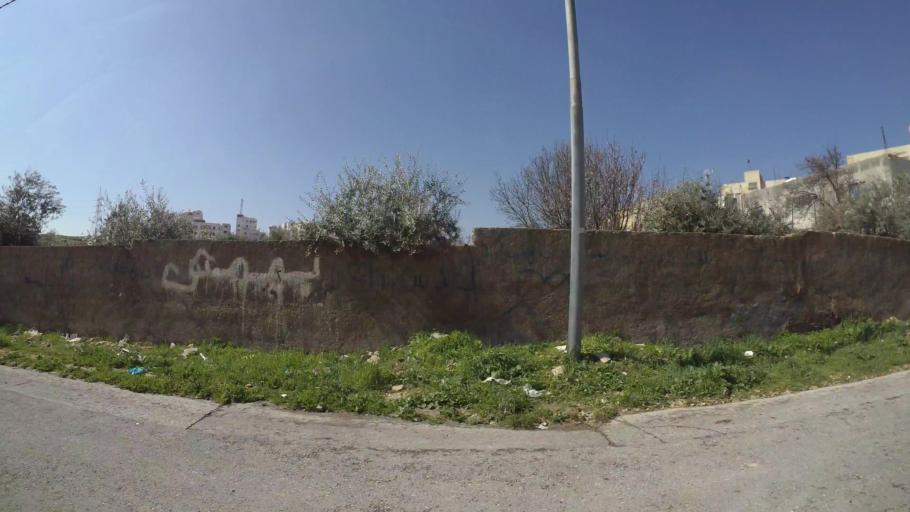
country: JO
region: Amman
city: Al Bunayyat ash Shamaliyah
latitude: 31.8965
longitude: 35.9009
